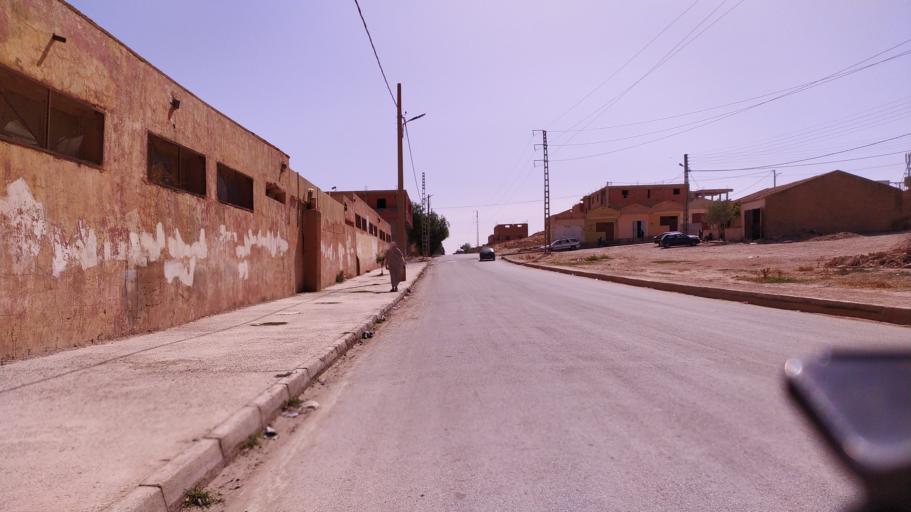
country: DZ
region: Tiaret
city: Frenda
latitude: 34.8929
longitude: 1.2418
